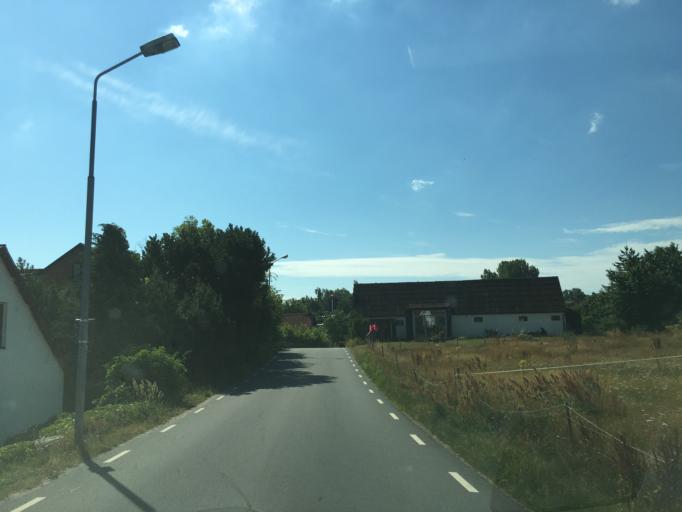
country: SE
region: Skane
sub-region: Simrishamns Kommun
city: Simrishamn
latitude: 55.5933
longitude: 14.3121
